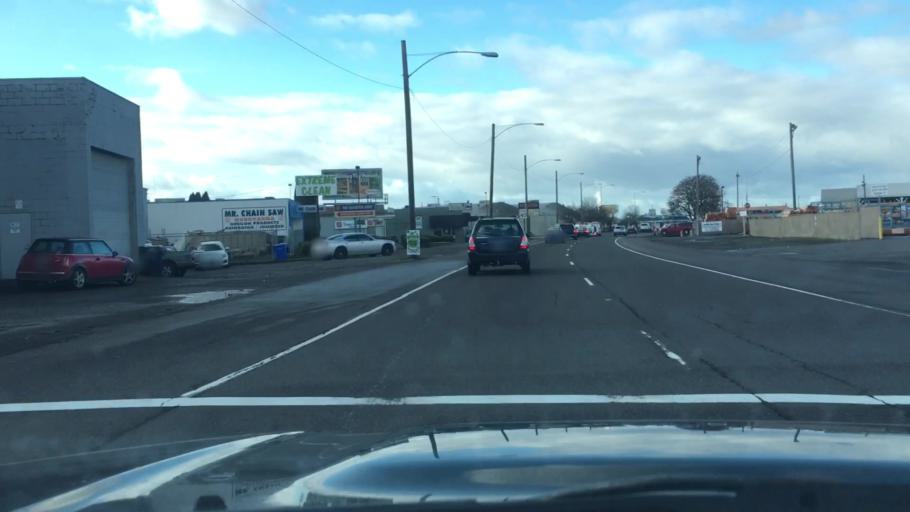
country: US
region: Oregon
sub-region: Lane County
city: Eugene
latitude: 44.0534
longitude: -123.1229
